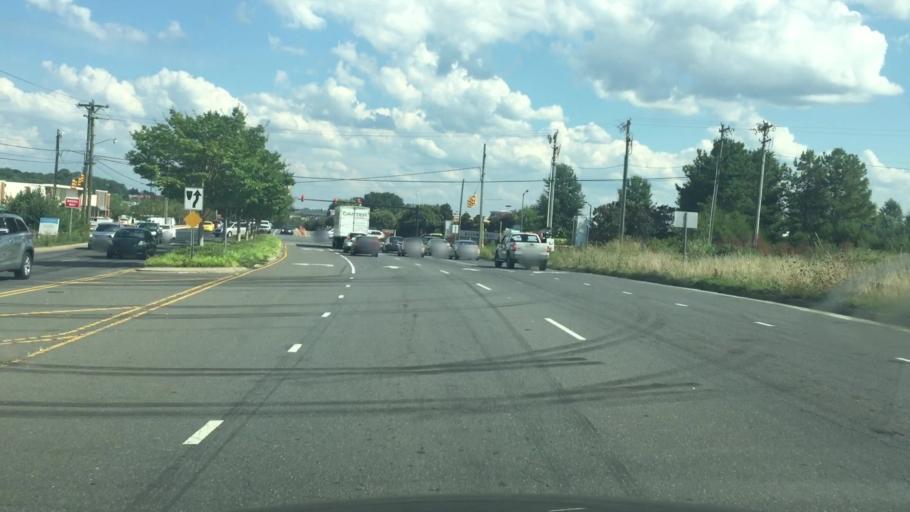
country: US
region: North Carolina
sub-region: Cabarrus County
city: Kannapolis
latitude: 35.4230
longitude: -80.6772
